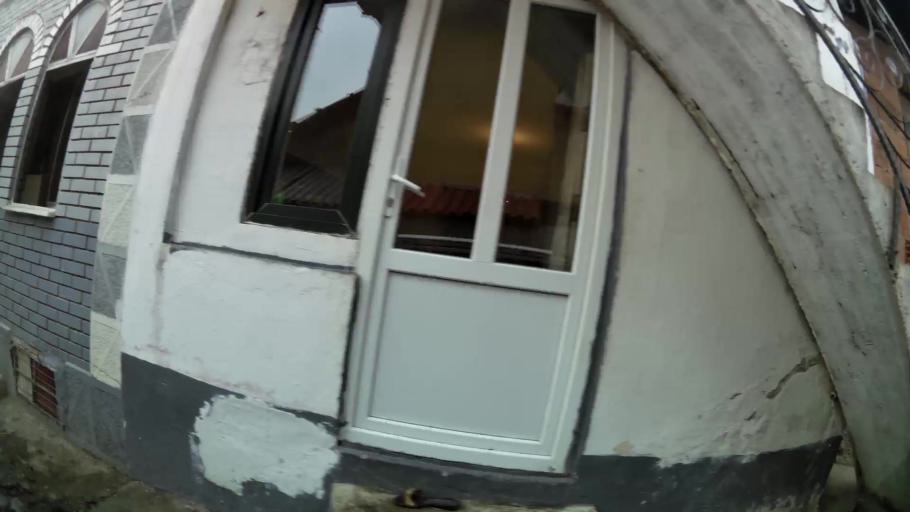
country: MK
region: Suto Orizari
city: Suto Orizare
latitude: 42.0453
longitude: 21.4219
